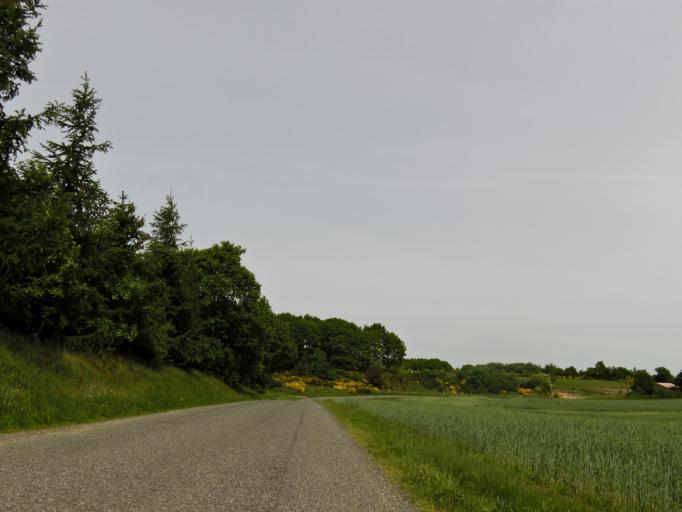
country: DK
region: Central Jutland
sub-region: Holstebro Kommune
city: Vinderup
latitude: 56.5454
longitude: 8.8822
